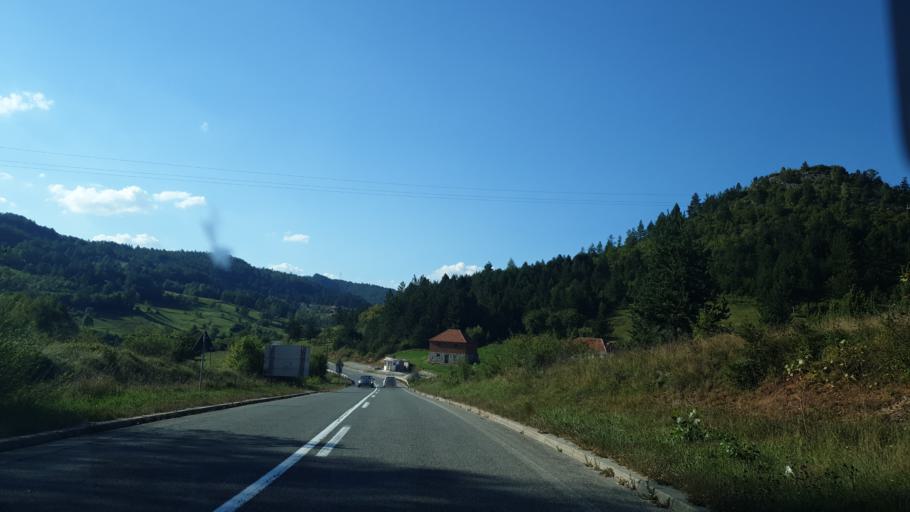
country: RS
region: Central Serbia
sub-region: Zlatiborski Okrug
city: Nova Varos
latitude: 43.5450
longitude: 19.7864
